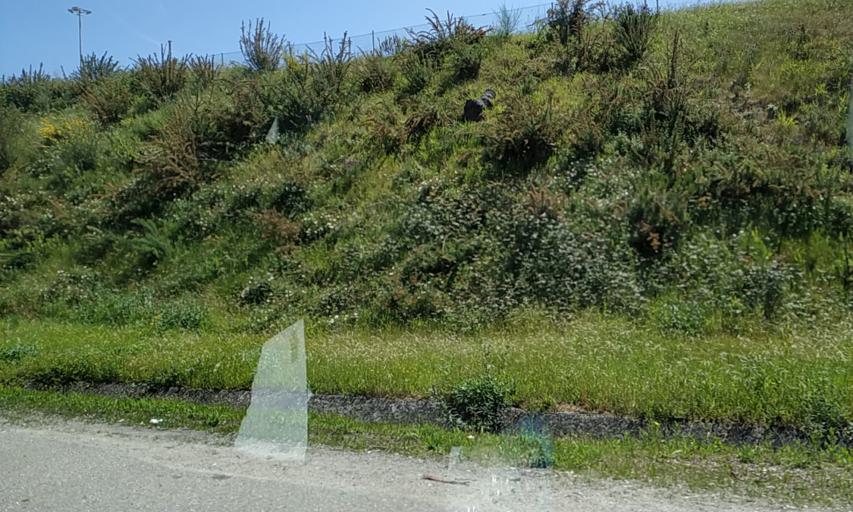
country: PT
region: Aveiro
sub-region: Aveiro
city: Aveiro
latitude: 40.6517
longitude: -8.6214
